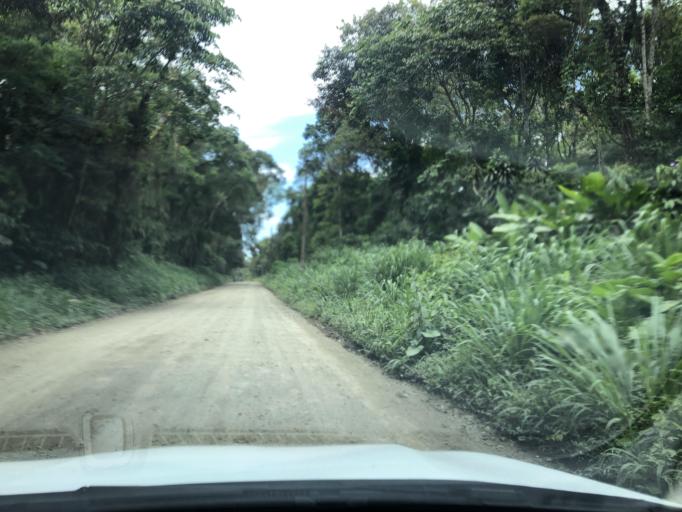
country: BR
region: Santa Catarina
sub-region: Sao Francisco Do Sul
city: Sao Francisco do Sul
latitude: -26.2264
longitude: -48.5975
